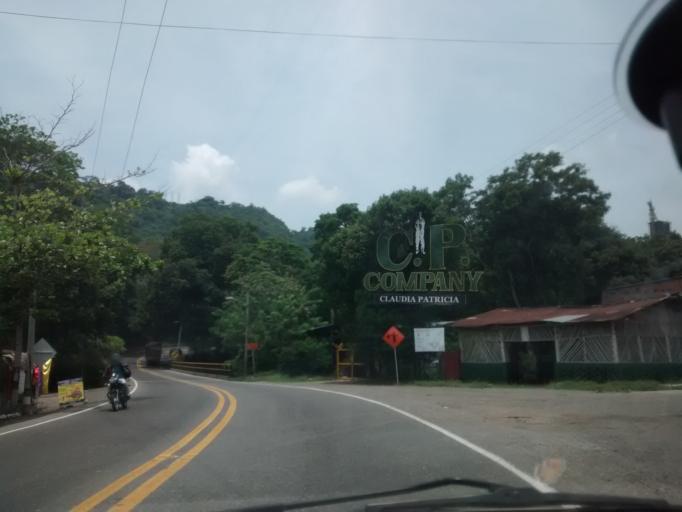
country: CO
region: Tolima
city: Valle de San Juan
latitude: 4.2869
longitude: -75.0337
